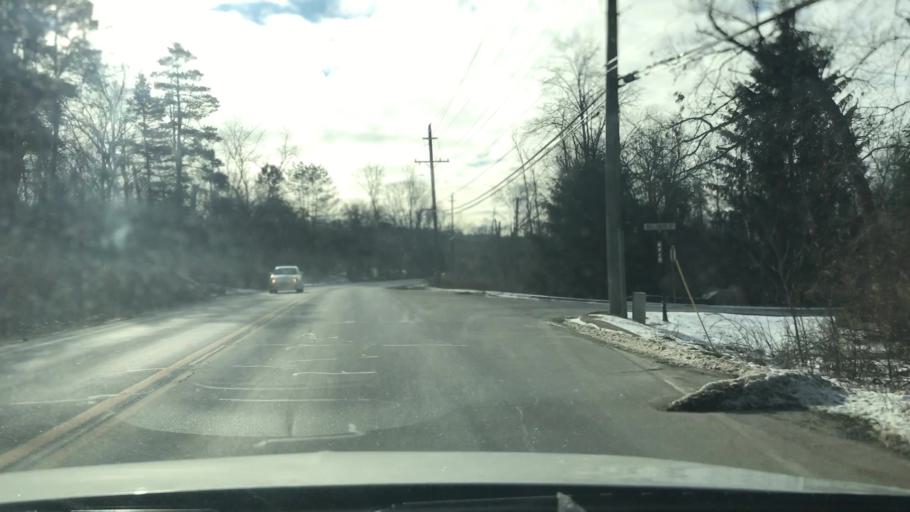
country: US
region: Michigan
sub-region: Oakland County
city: Rochester
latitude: 42.7283
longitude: -83.1572
